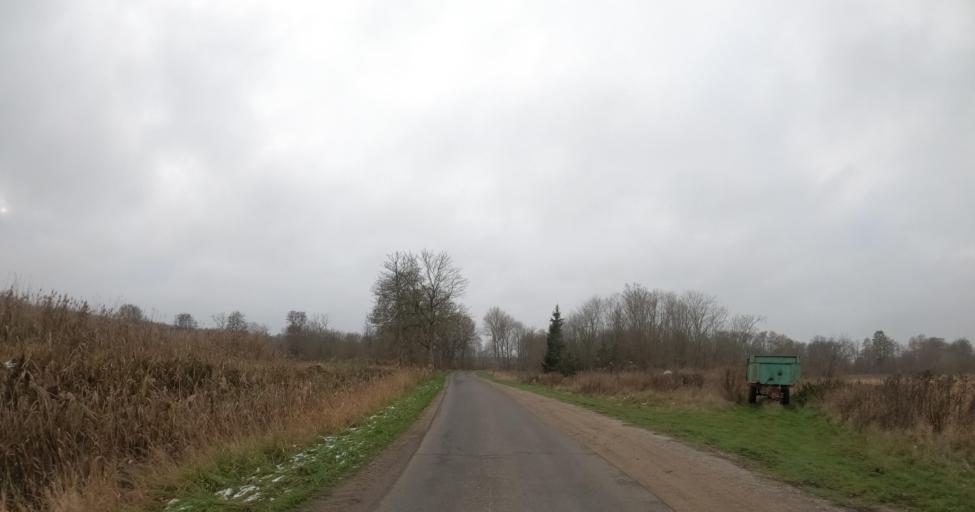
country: PL
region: West Pomeranian Voivodeship
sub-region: Powiat bialogardzki
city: Karlino
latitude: 53.9809
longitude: 15.8913
